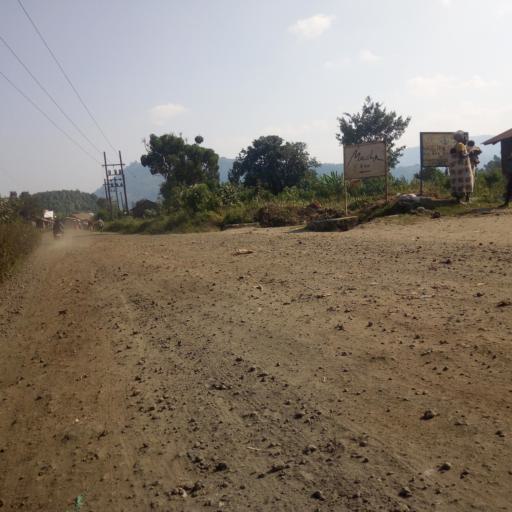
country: UG
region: Western Region
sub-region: Kisoro District
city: Kisoro
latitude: -1.2337
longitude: 29.7121
